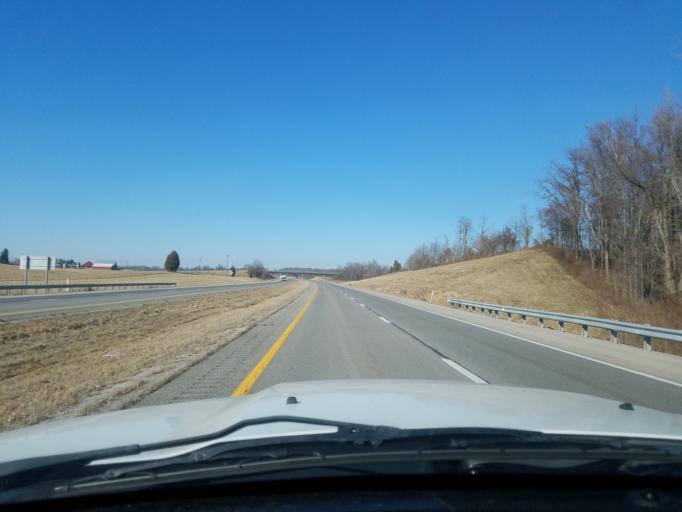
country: US
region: Kentucky
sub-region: Daviess County
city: Masonville
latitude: 37.7144
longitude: -87.0488
